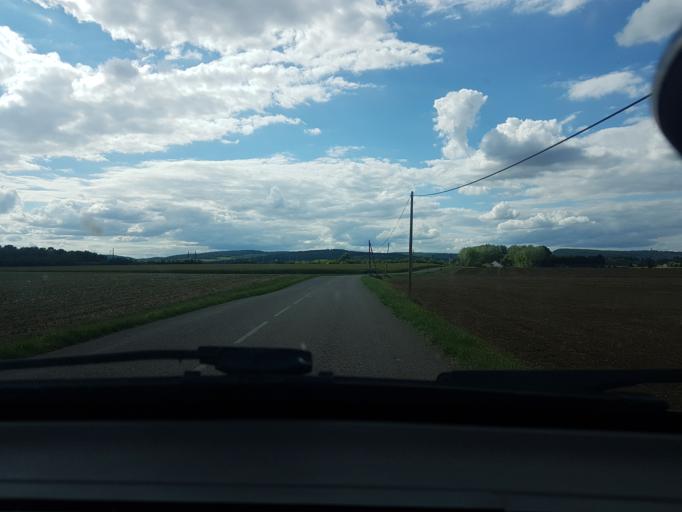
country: FR
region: Bourgogne
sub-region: Departement de Saone-et-Loire
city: Fontaines
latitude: 46.8431
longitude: 4.7883
